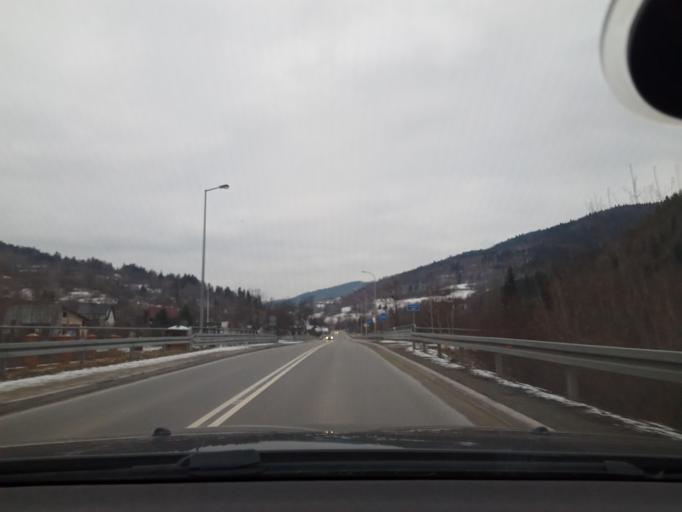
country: PL
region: Lesser Poland Voivodeship
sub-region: Powiat limanowski
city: Kamienica
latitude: 49.5842
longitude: 20.3256
